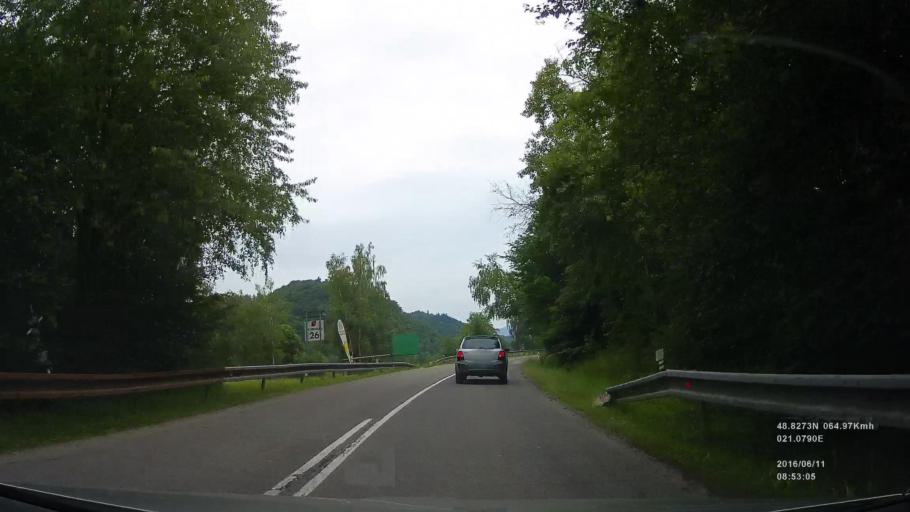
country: SK
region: Kosicky
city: Gelnica
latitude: 48.8224
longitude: 21.0810
